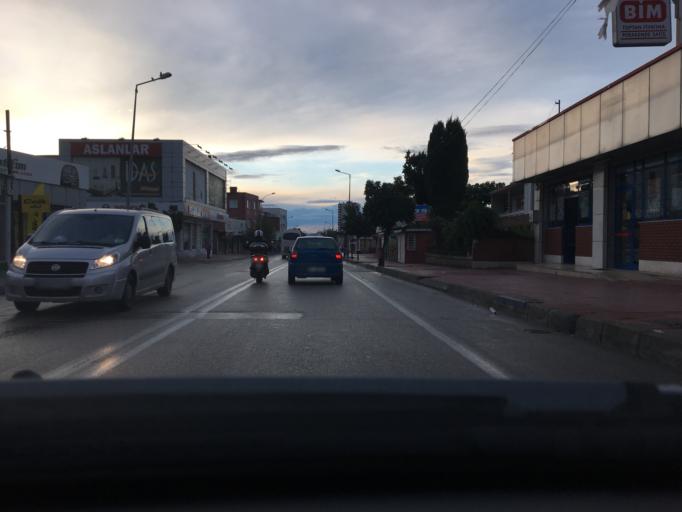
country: TR
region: Adana
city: Seyhan
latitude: 37.0159
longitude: 35.3007
